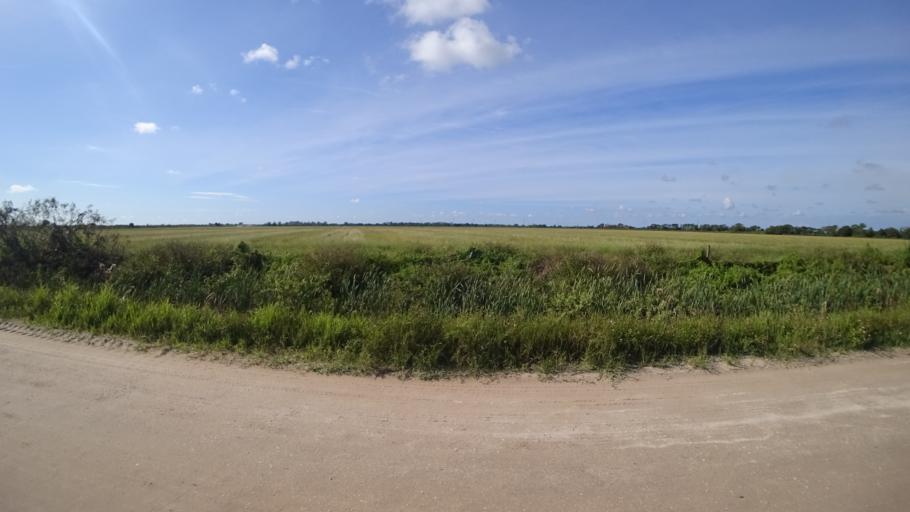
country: US
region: Florida
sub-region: Sarasota County
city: The Meadows
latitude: 27.4689
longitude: -82.3410
